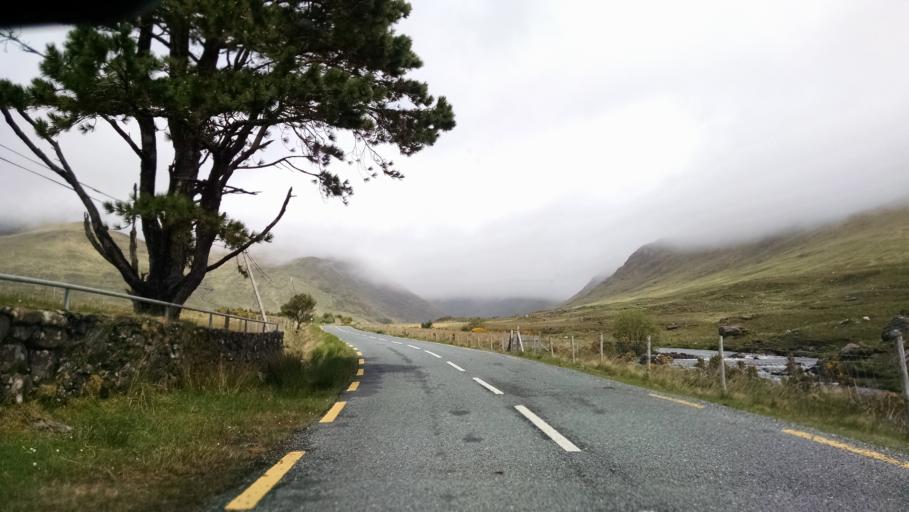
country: IE
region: Connaught
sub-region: County Galway
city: Clifden
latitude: 53.6134
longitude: -9.7513
